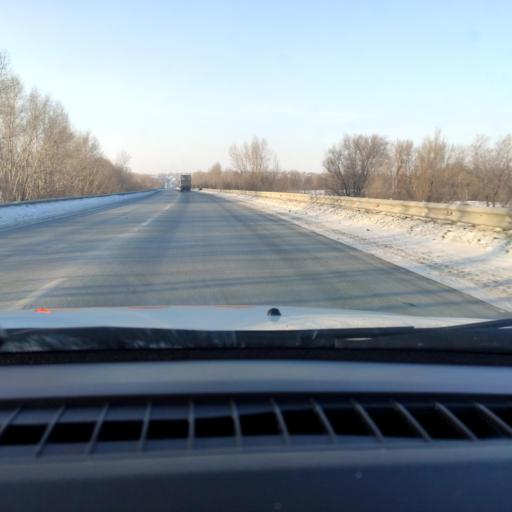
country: RU
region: Samara
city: Smyshlyayevka
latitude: 53.2178
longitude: 50.5022
